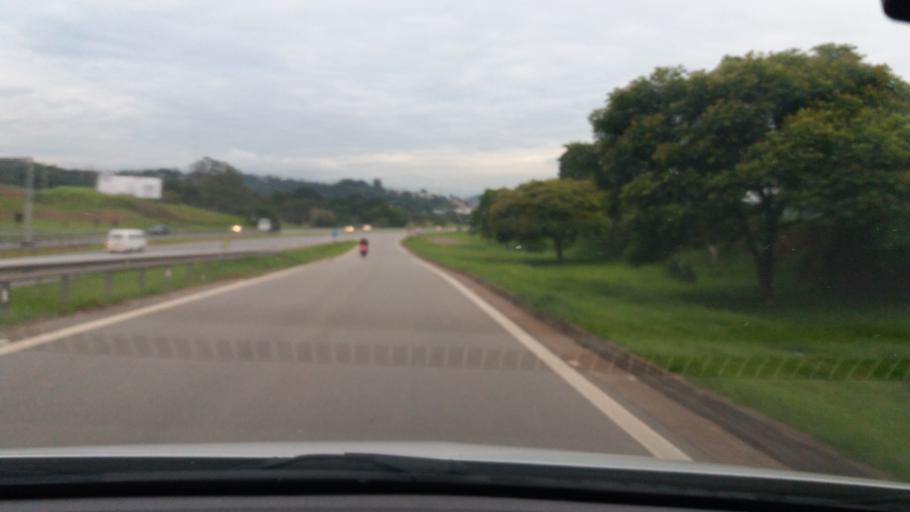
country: BR
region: Sao Paulo
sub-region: Bom Jesus Dos Perdoes
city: Bom Jesus dos Perdoes
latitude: -23.1567
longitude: -46.4504
